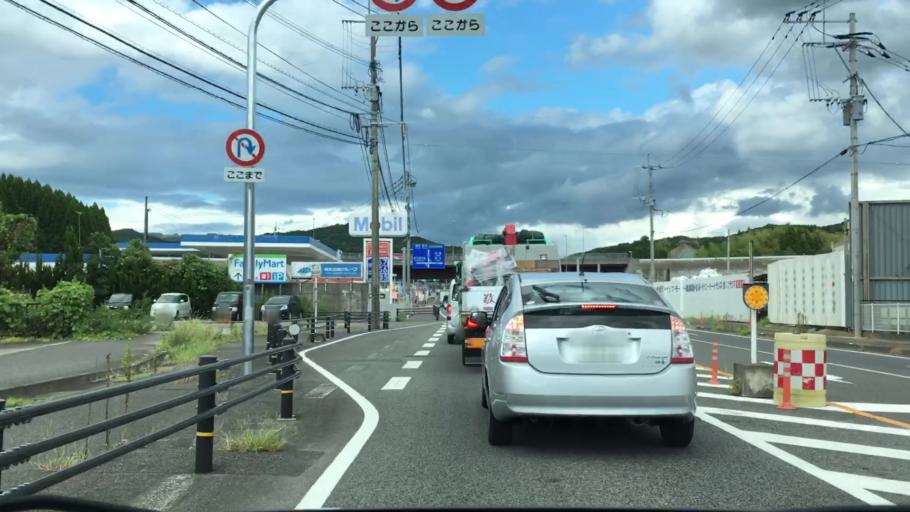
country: JP
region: Saga Prefecture
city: Imaricho-ko
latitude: 33.2804
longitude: 129.8958
